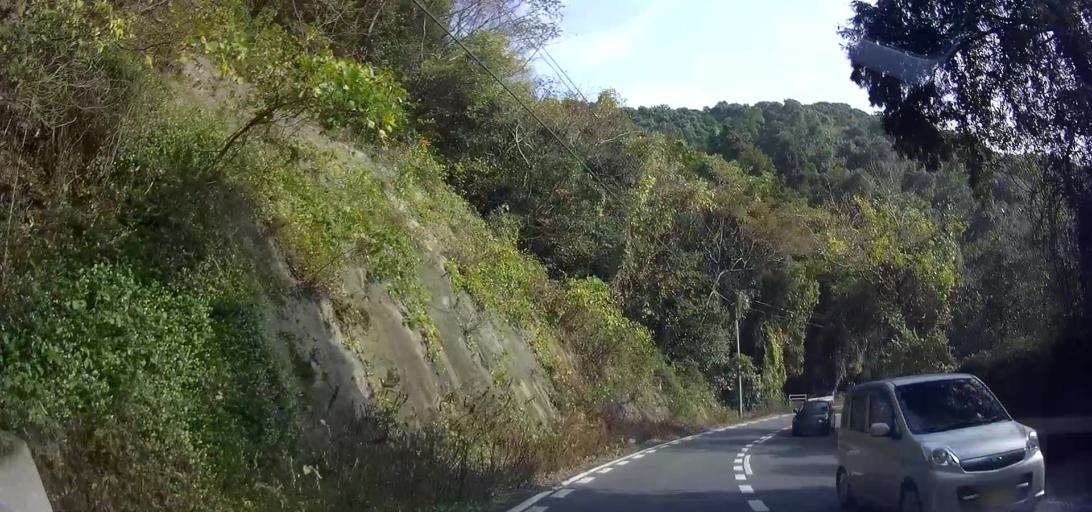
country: JP
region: Nagasaki
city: Shimabara
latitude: 32.6773
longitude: 130.2051
